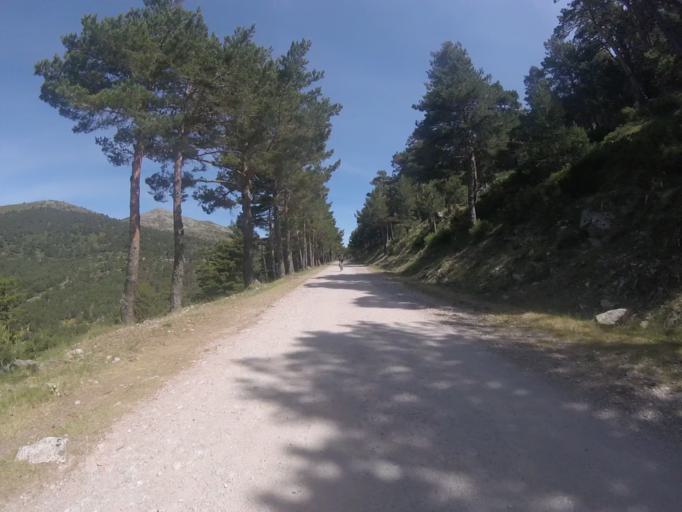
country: ES
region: Madrid
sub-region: Provincia de Madrid
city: Cercedilla
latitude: 40.7880
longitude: -4.0591
